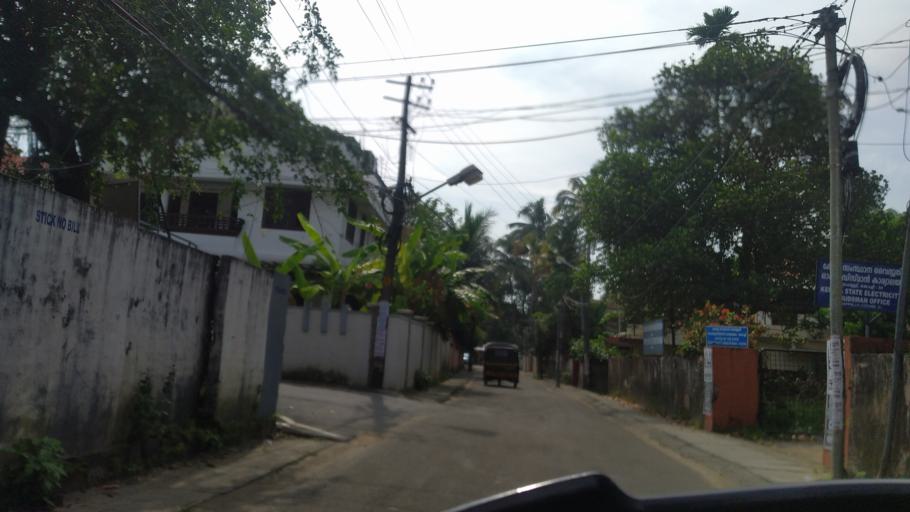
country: IN
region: Kerala
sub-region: Ernakulam
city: Elur
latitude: 10.0113
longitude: 76.3092
